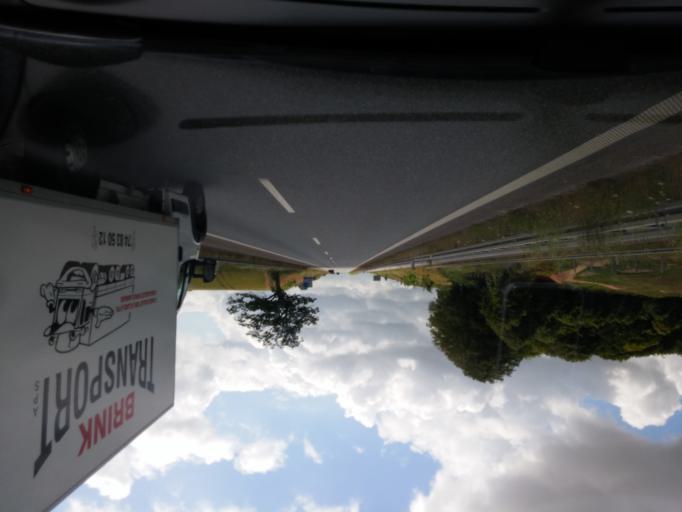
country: DK
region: South Denmark
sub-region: Faaborg-Midtfyn Kommune
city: Ringe
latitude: 55.2310
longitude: 10.4953
